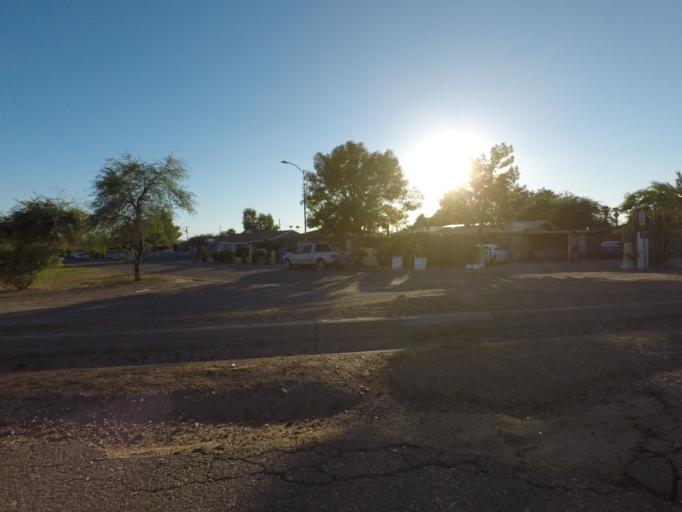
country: US
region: Arizona
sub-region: Maricopa County
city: Phoenix
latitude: 33.4710
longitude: -112.0231
